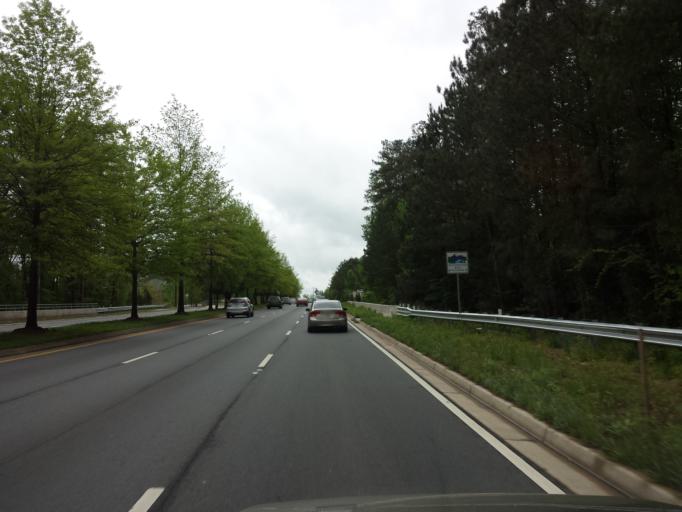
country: US
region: Georgia
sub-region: Cobb County
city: Kennesaw
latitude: 33.9767
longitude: -84.6105
